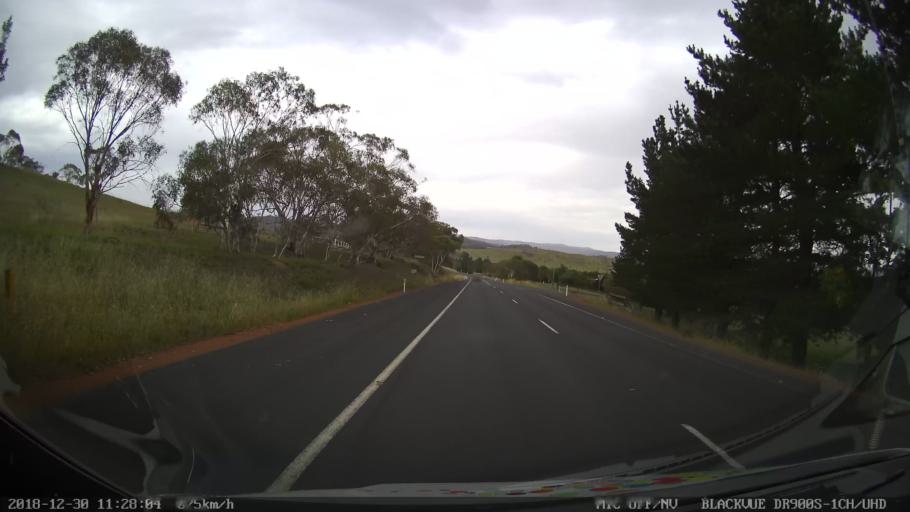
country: AU
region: New South Wales
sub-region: Snowy River
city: Jindabyne
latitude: -36.4553
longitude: 148.6217
